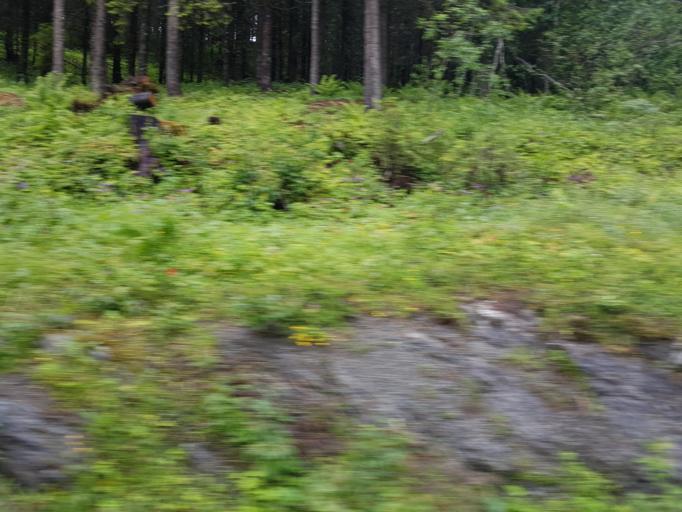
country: NO
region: Sor-Trondelag
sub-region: Selbu
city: Mebonden
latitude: 63.3046
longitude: 11.0785
